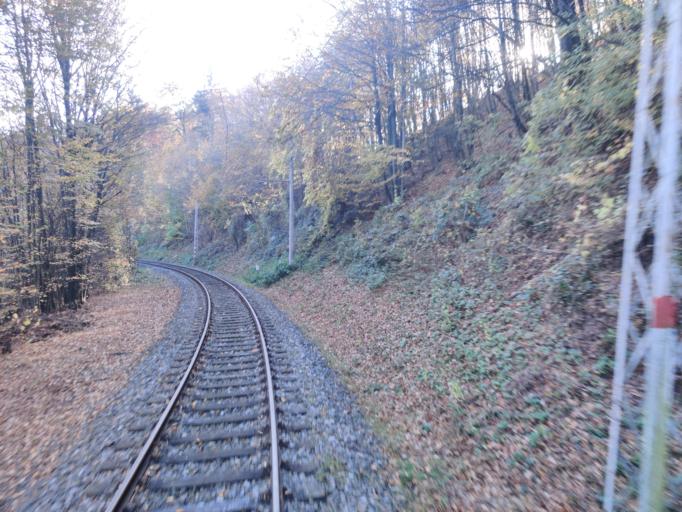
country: AT
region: Styria
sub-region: Politischer Bezirk Suedoststeiermark
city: Maierdorf
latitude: 46.9295
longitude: 15.8534
